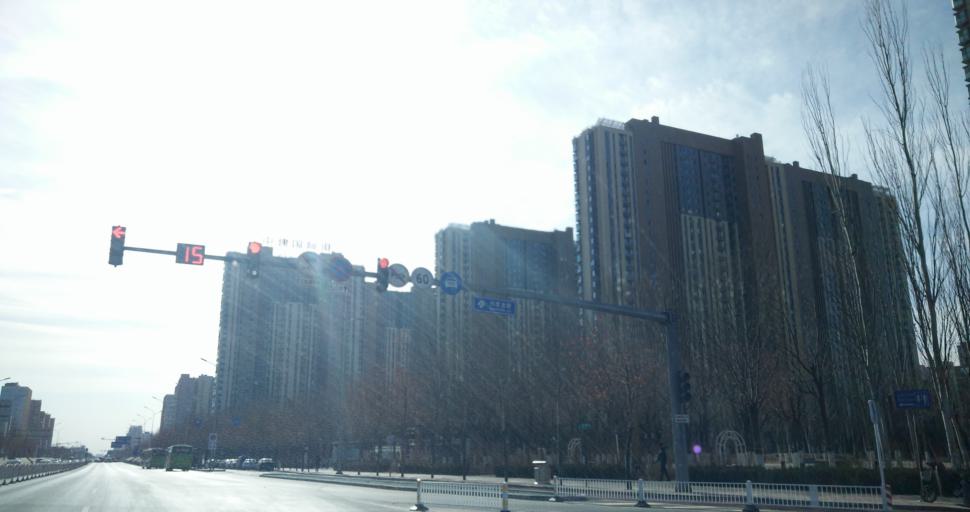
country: CN
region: Beijing
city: Daxing
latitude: 39.7563
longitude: 116.3260
